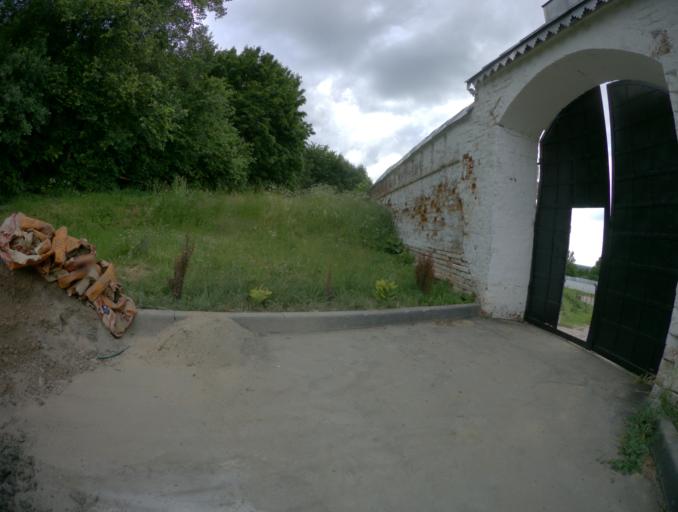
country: RU
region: Vladimir
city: Gorokhovets
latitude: 56.2039
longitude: 42.6729
